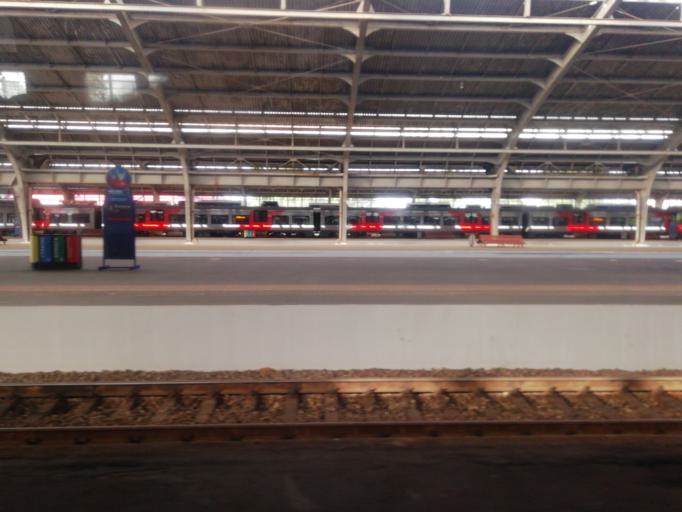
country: RU
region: Kaliningrad
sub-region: Gorod Kaliningrad
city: Kaliningrad
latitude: 54.6935
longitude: 20.4985
